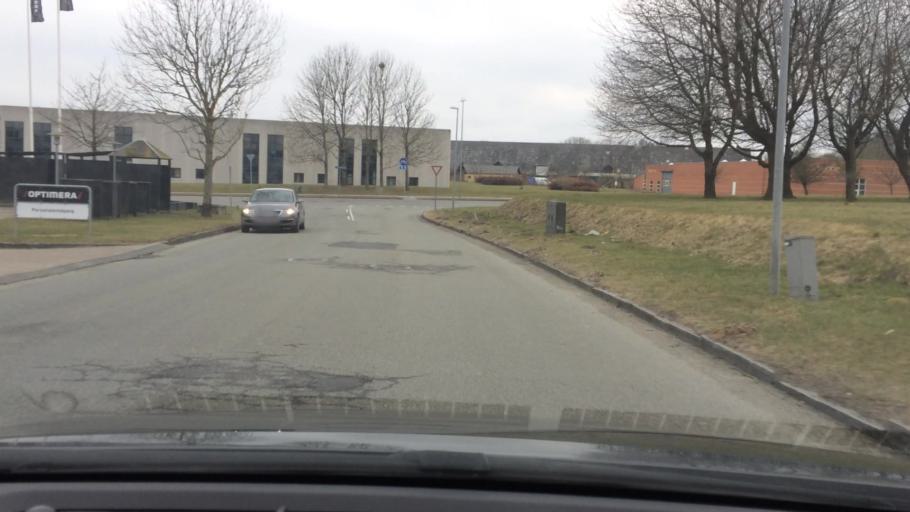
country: DK
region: South Denmark
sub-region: Vejle Kommune
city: Vejle
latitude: 55.7317
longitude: 9.5673
